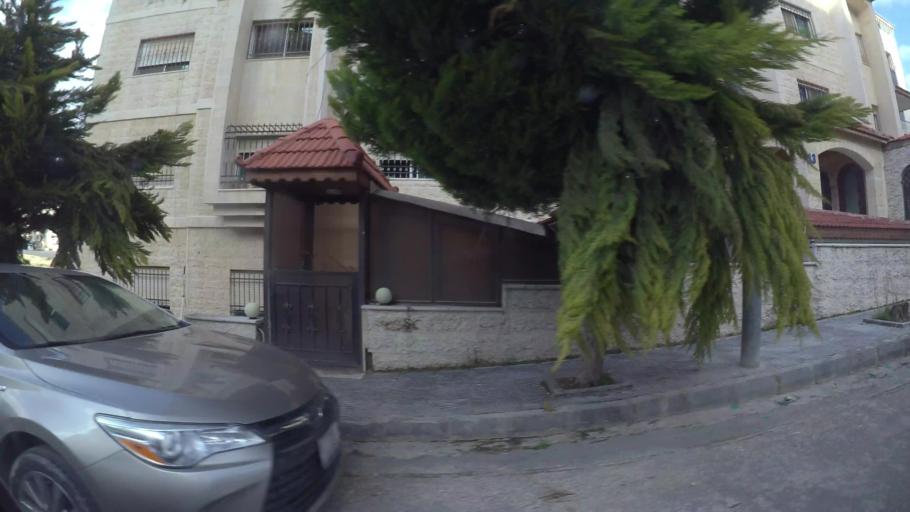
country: JO
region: Amman
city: Al Jubayhah
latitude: 32.0080
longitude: 35.8609
